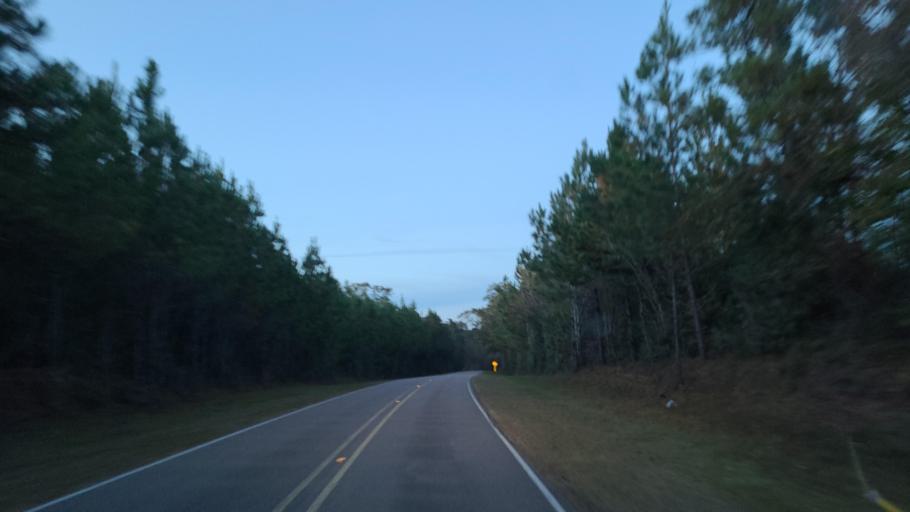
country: US
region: Mississippi
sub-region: Perry County
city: New Augusta
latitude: 31.1398
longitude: -89.2014
